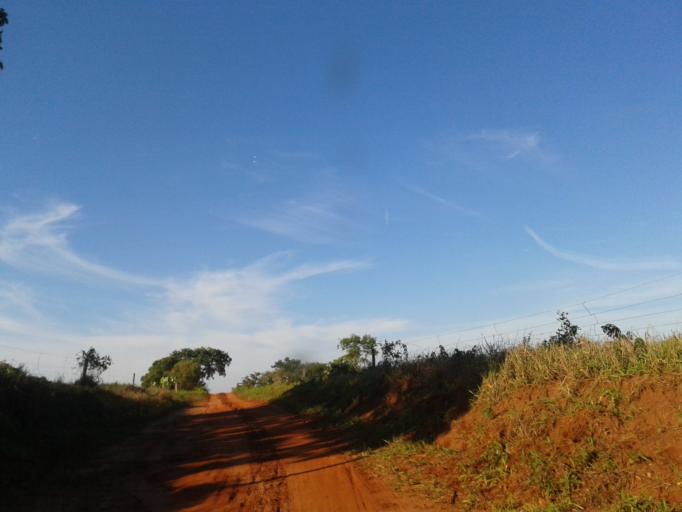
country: BR
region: Minas Gerais
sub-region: Santa Vitoria
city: Santa Vitoria
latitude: -18.9774
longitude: -49.8914
